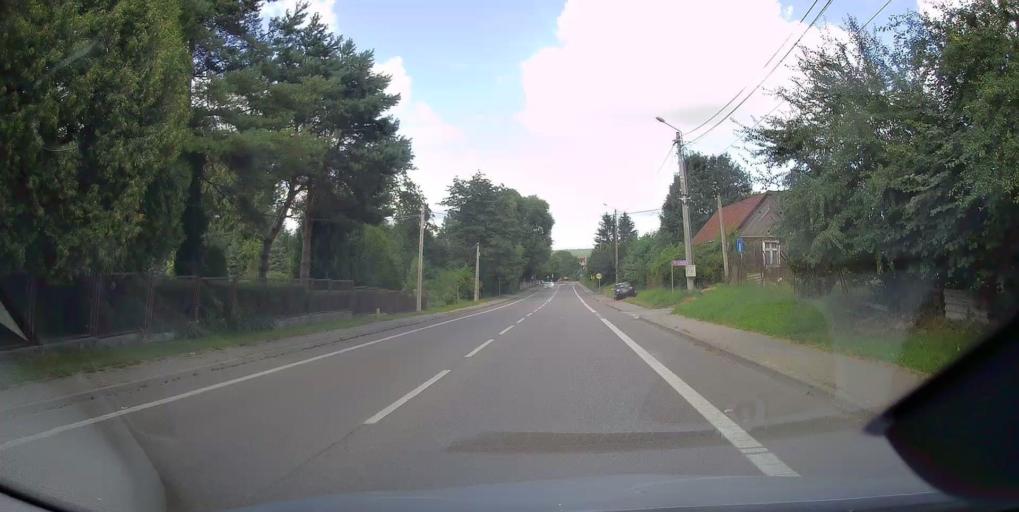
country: PL
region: Swietokrzyskie
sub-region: Powiat kielecki
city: Nowa Slupia
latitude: 50.8606
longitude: 21.0894
